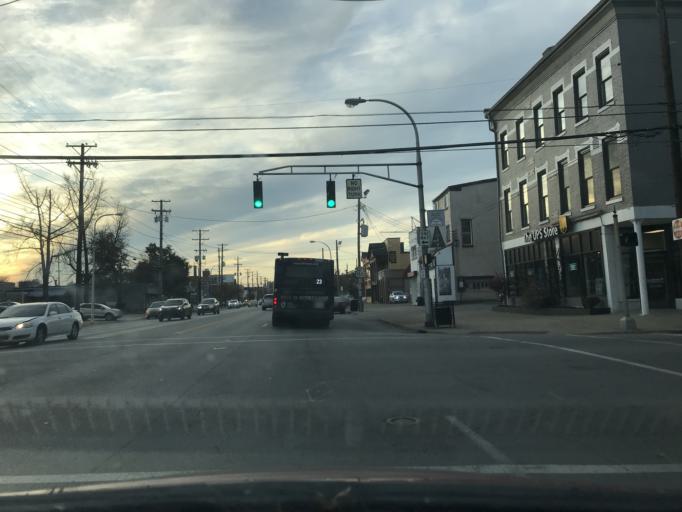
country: US
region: Kentucky
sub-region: Jefferson County
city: Louisville
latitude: 38.2447
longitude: -85.7394
